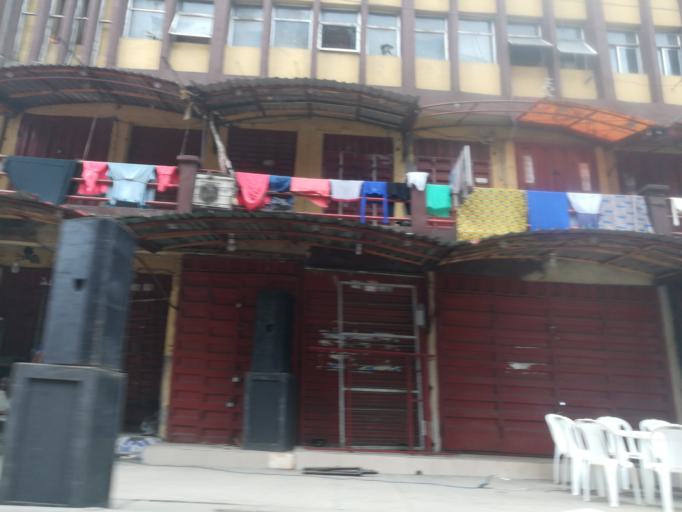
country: NG
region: Lagos
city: Lagos
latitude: 6.4547
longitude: 3.3888
